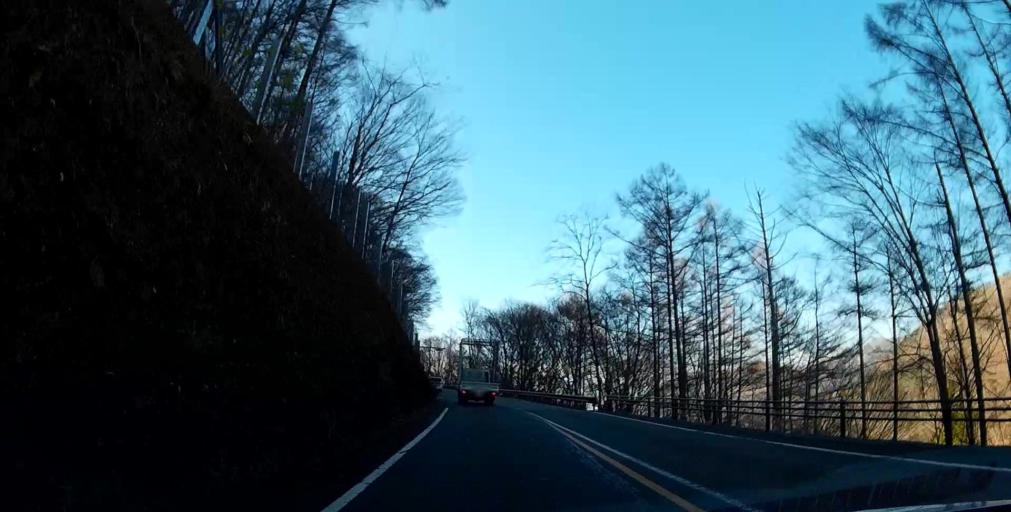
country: JP
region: Yamanashi
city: Fujikawaguchiko
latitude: 35.5732
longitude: 138.7689
